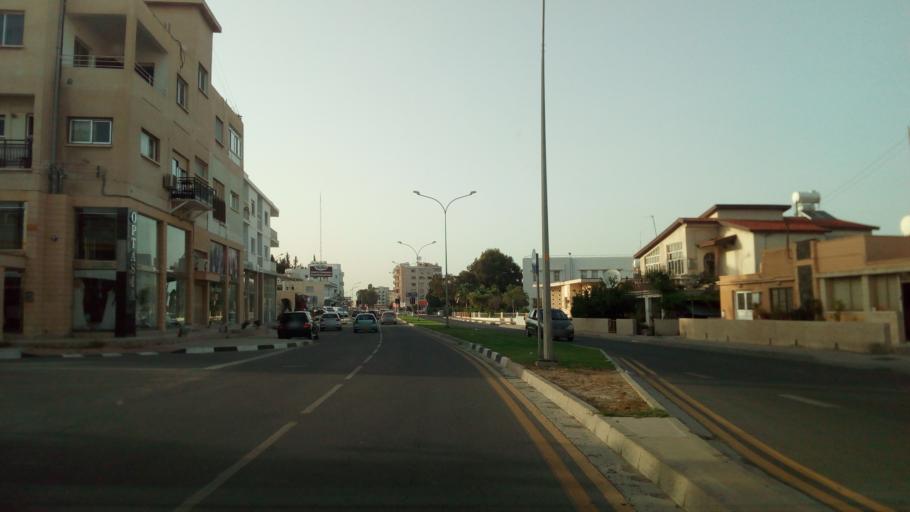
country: CY
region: Larnaka
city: Larnaca
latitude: 34.9211
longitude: 33.6166
